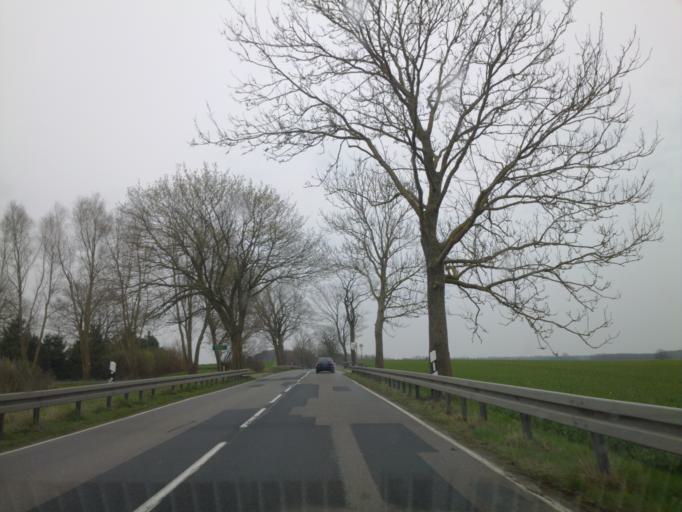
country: DE
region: Mecklenburg-Vorpommern
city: Barth
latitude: 54.3071
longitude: 12.7178
